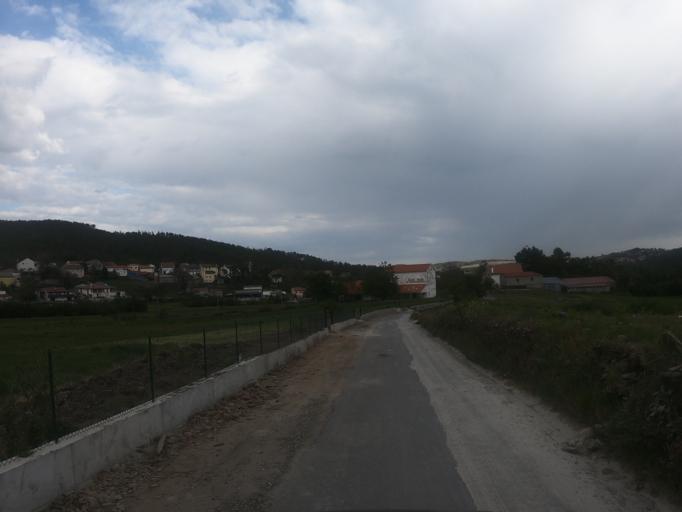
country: PT
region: Vila Real
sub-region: Santa Marta de Penaguiao
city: Santa Marta de Penaguiao
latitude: 41.3018
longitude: -7.8759
